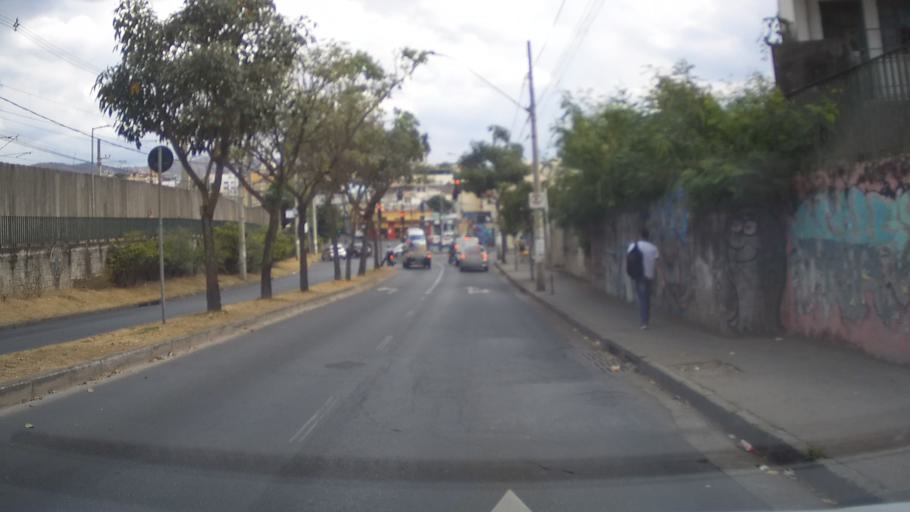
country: BR
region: Minas Gerais
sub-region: Belo Horizonte
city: Belo Horizonte
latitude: -19.9071
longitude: -43.9136
